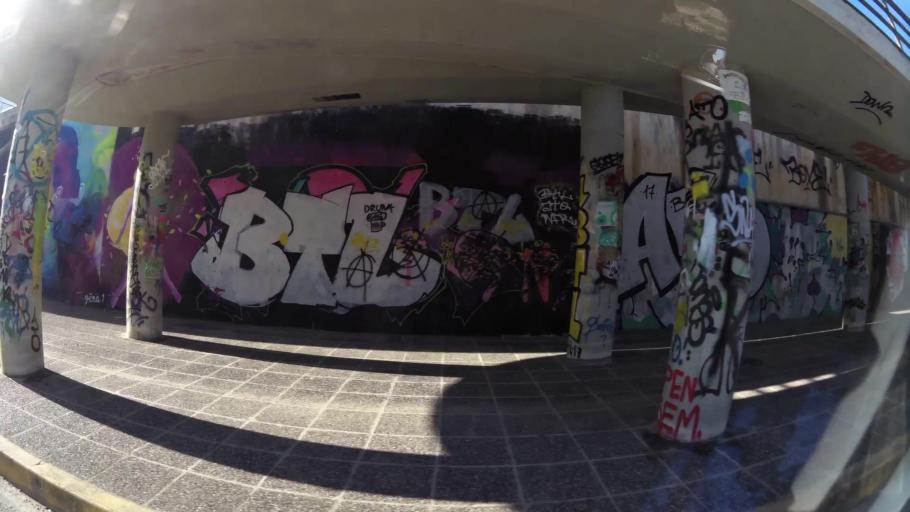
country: GR
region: Attica
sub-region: Nomarchia Athinas
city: Irakleio
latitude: 38.0538
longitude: 23.7785
